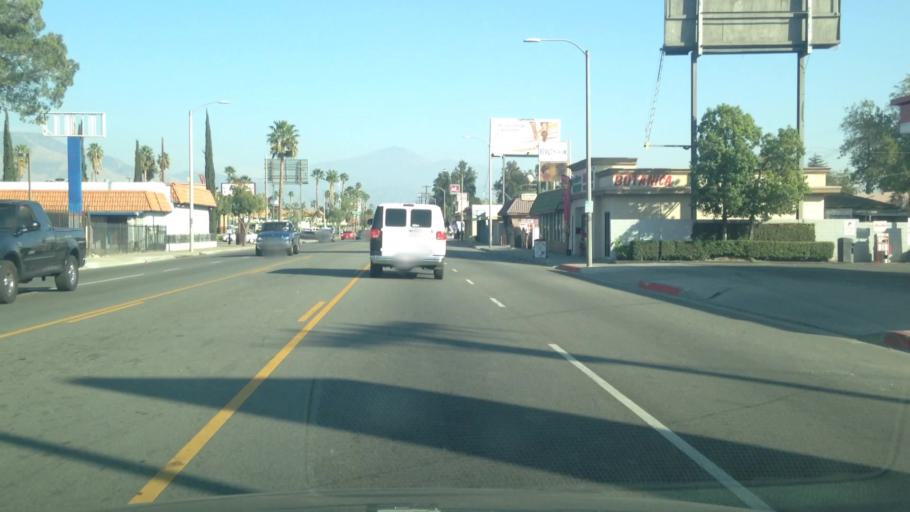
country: US
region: California
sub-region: San Bernardino County
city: San Bernardino
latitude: 34.1213
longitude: -117.2813
